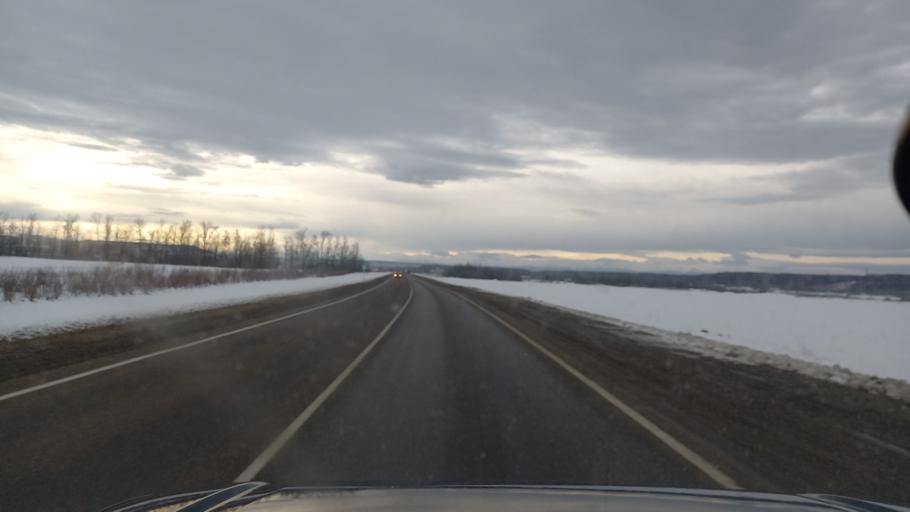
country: RU
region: Adygeya
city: Maykop
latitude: 44.6217
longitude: 40.0395
